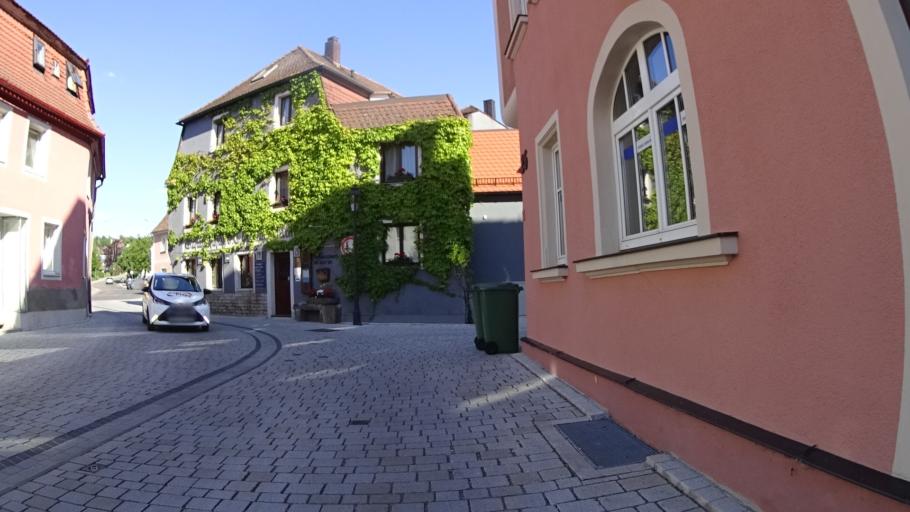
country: DE
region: Bavaria
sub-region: Regierungsbezirk Mittelfranken
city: Feuchtwangen
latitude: 49.1669
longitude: 10.3330
